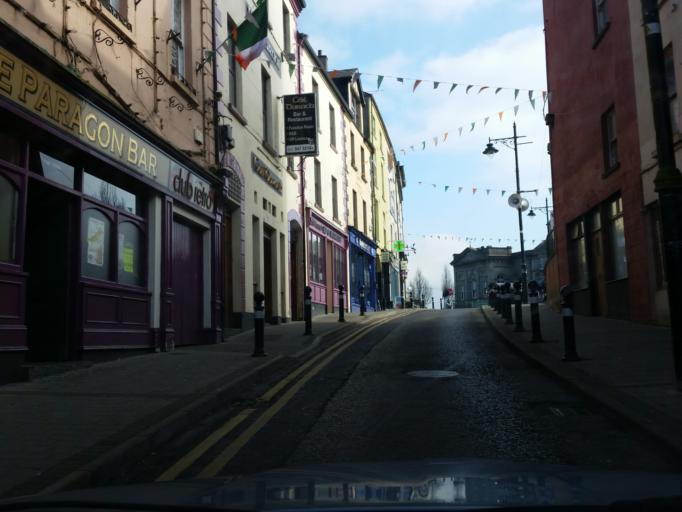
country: IE
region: Ulster
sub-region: County Monaghan
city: Clones
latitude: 54.1799
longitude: -7.2326
